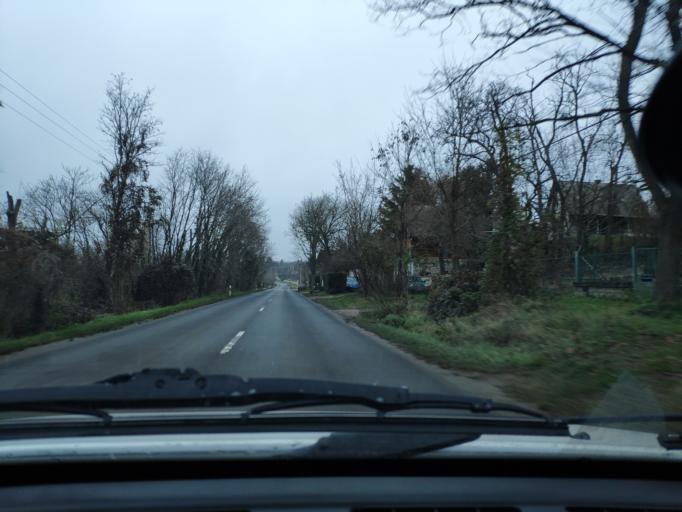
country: HU
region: Pest
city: Soskut
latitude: 47.4222
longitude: 18.8260
